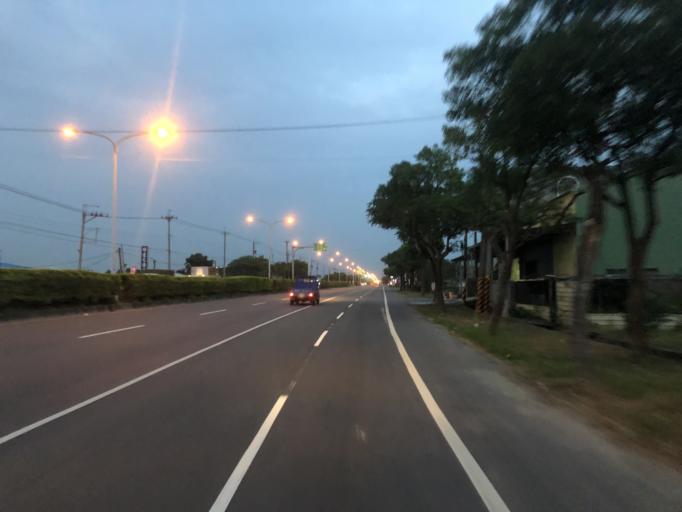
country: TW
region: Taiwan
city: Yujing
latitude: 23.1418
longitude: 120.3248
